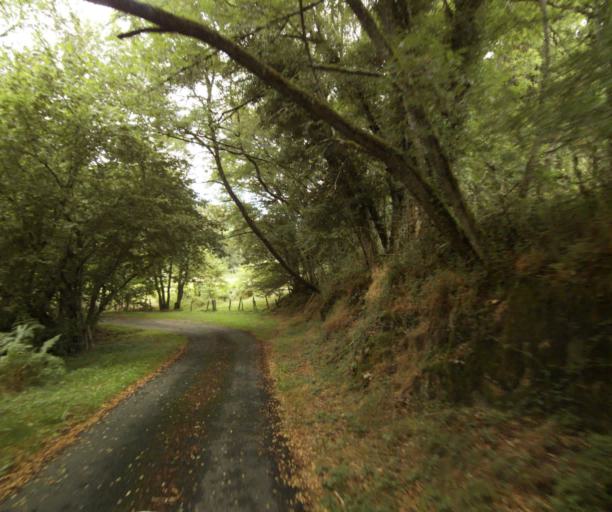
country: FR
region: Limousin
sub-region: Departement de la Correze
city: Sainte-Fortunade
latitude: 45.1762
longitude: 1.8128
